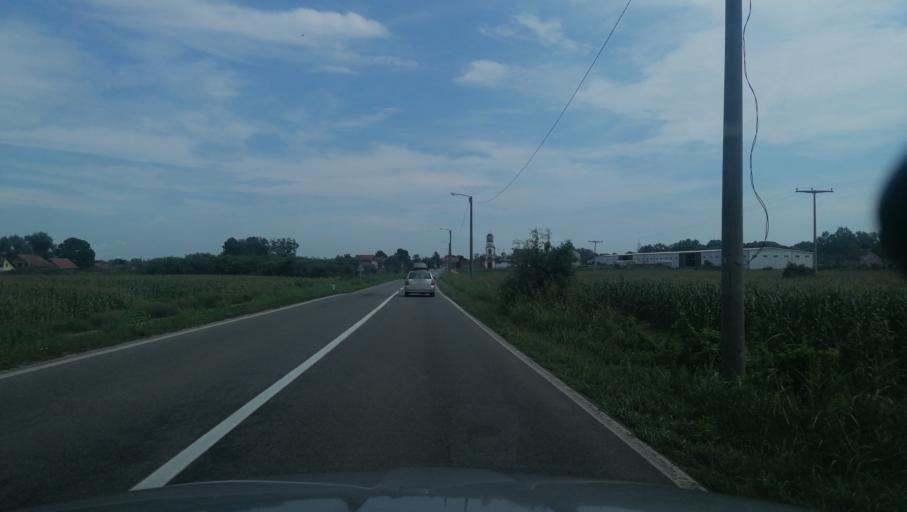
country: BA
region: Brcko
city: Brka
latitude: 44.9278
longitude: 18.7210
